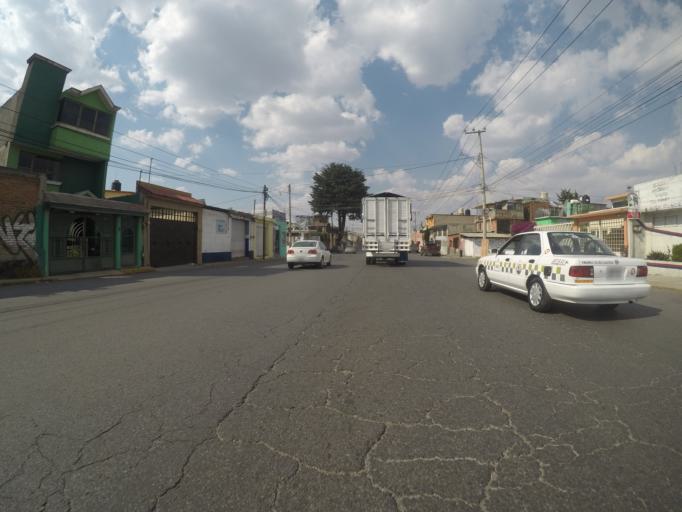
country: MX
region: Mexico
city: San Buenaventura
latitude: 19.2617
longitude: -99.6595
